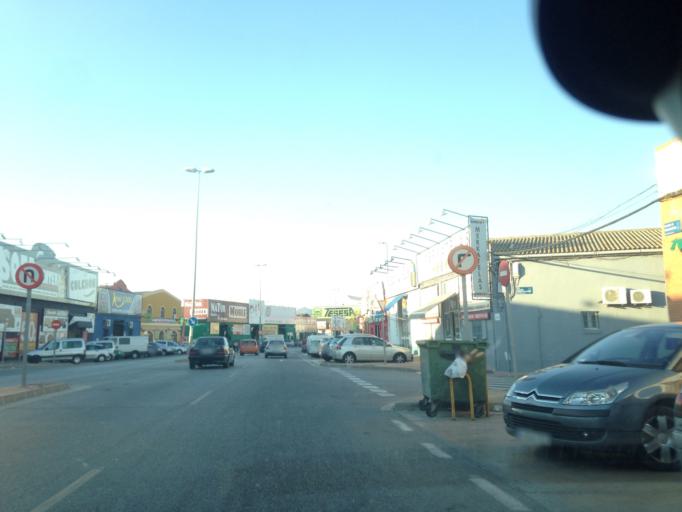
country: ES
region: Andalusia
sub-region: Provincia de Malaga
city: Malaga
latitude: 36.7097
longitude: -4.4825
